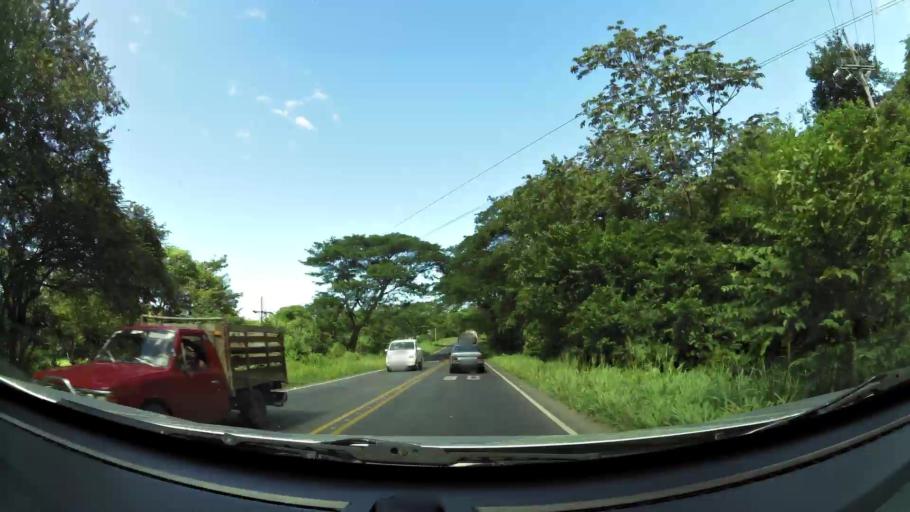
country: CR
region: Guanacaste
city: Juntas
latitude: 10.3114
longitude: -85.0418
